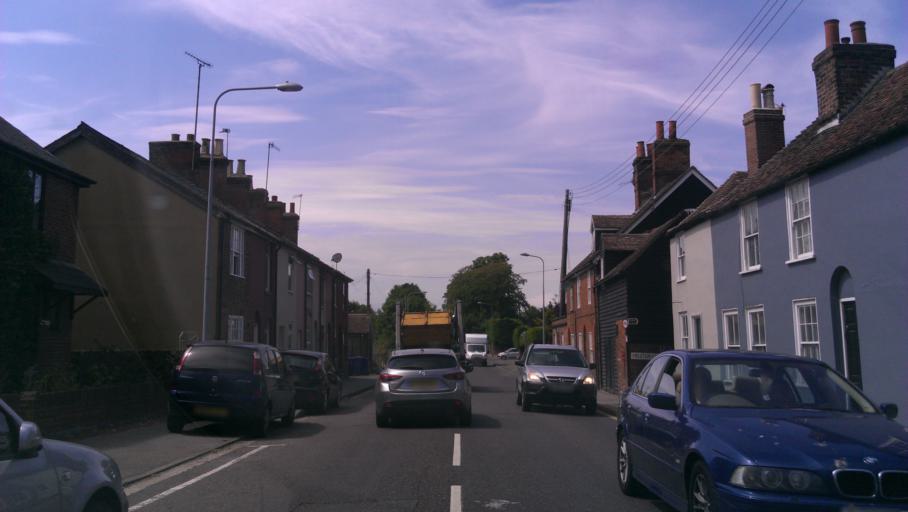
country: GB
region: England
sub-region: Kent
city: Faversham
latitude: 51.3077
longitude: 0.8941
